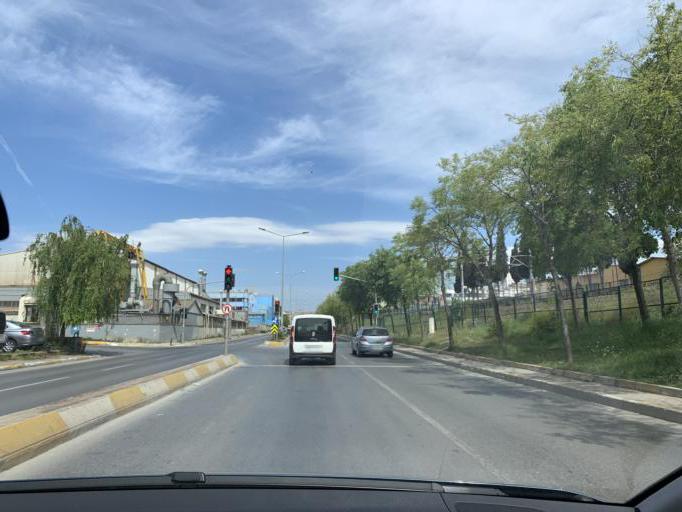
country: TR
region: Istanbul
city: Icmeler
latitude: 40.8501
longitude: 29.2945
